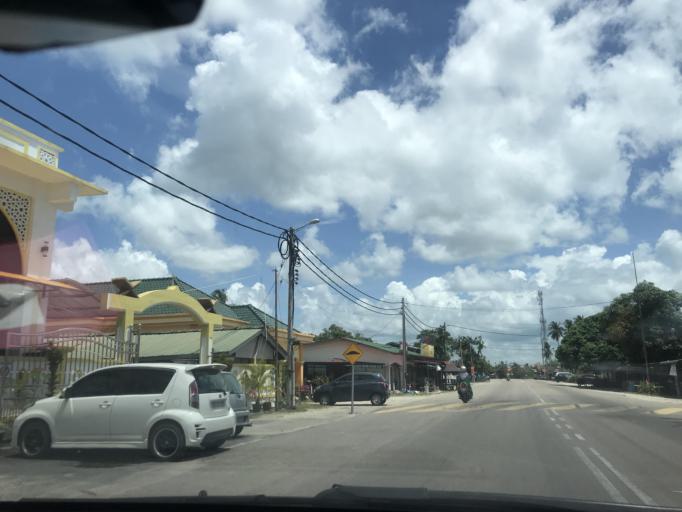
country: MY
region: Kelantan
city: Tumpat
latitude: 6.2218
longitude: 102.1095
